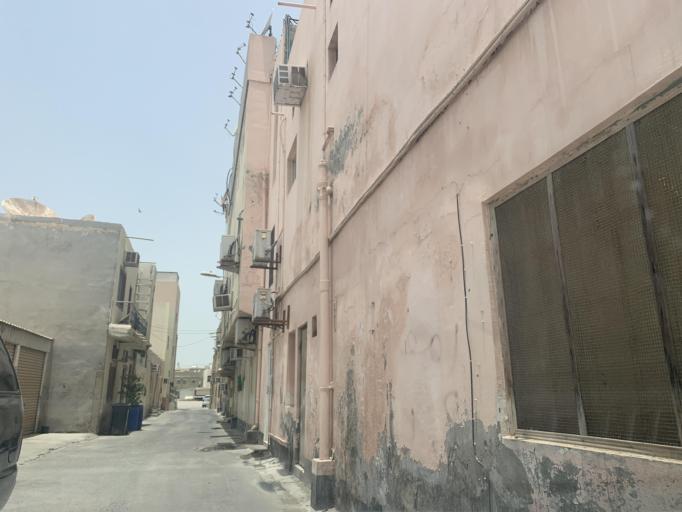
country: BH
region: Manama
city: Jidd Hafs
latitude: 26.2122
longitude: 50.5408
